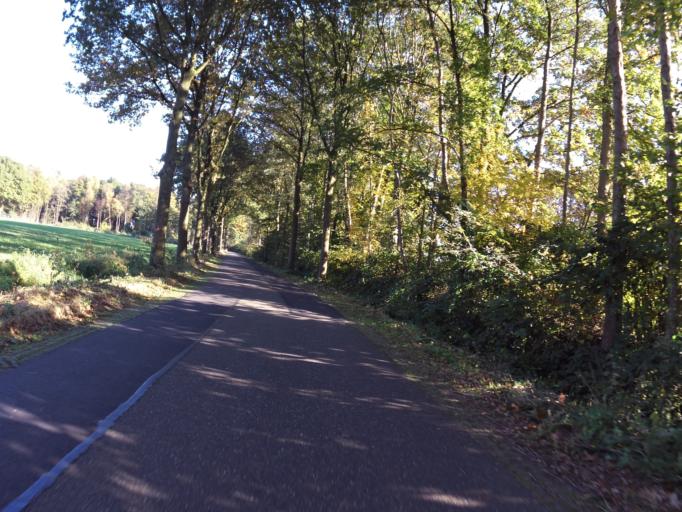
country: NL
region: North Brabant
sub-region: Gemeente Vught
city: Vught
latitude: 51.6213
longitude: 5.2908
